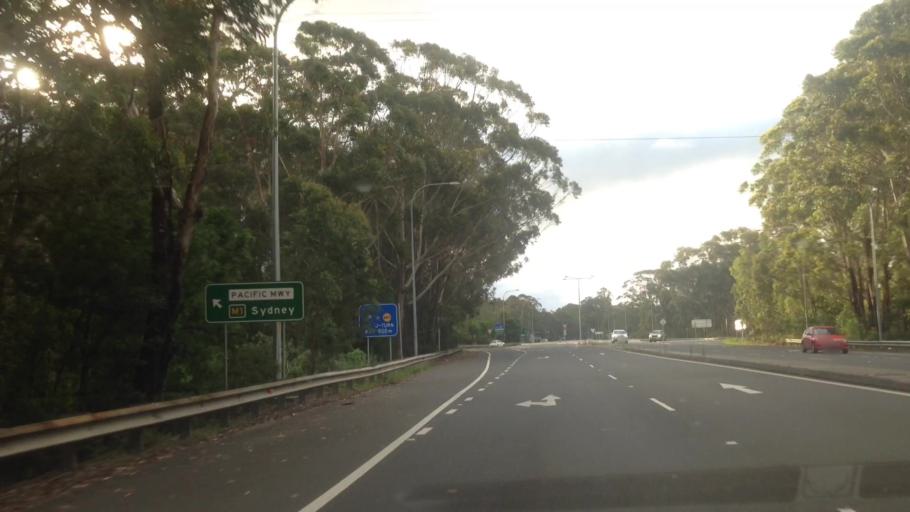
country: AU
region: New South Wales
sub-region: Wyong Shire
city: Chittaway Bay
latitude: -33.3054
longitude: 151.4051
